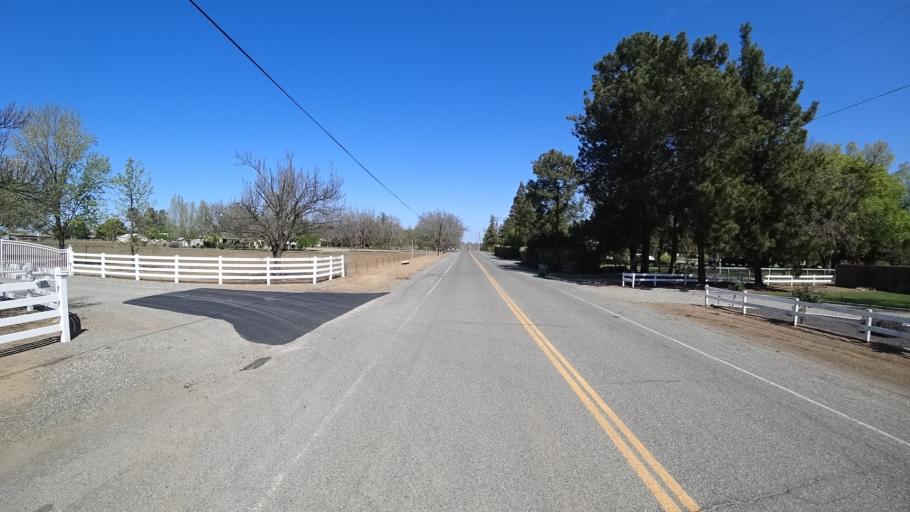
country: US
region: California
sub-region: Glenn County
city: Willows
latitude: 39.5360
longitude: -122.2075
